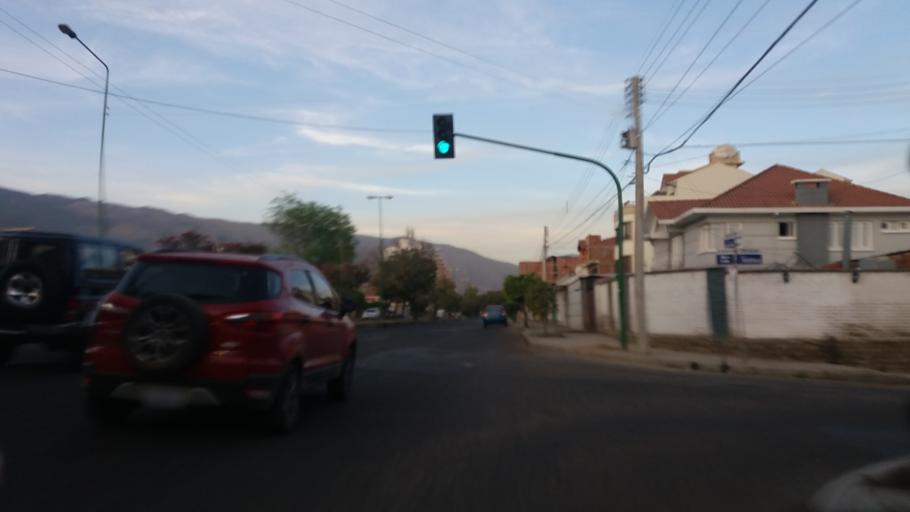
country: BO
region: Cochabamba
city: Cochabamba
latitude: -17.3830
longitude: -66.1796
